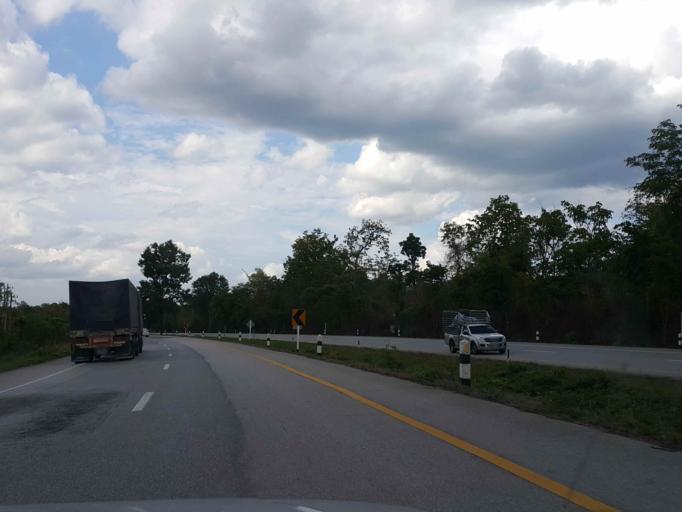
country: TH
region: Lampang
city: Thoen
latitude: 17.7576
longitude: 99.2407
